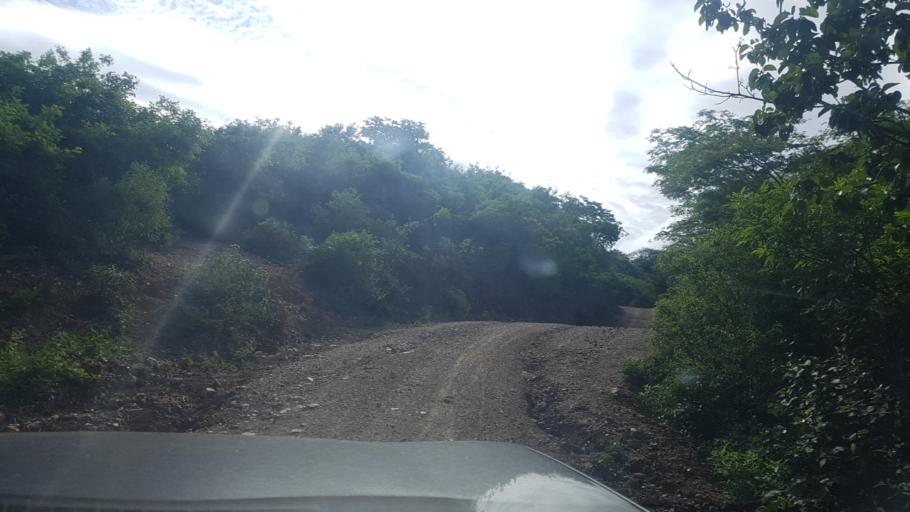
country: NI
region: Nueva Segovia
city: Ocotal
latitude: 13.6030
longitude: -86.4430
